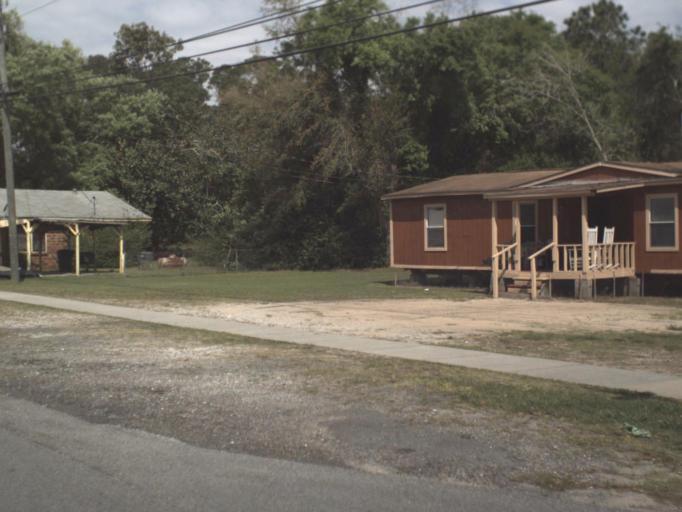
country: US
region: Florida
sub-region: Escambia County
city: Warrington
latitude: 30.3873
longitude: -87.2866
